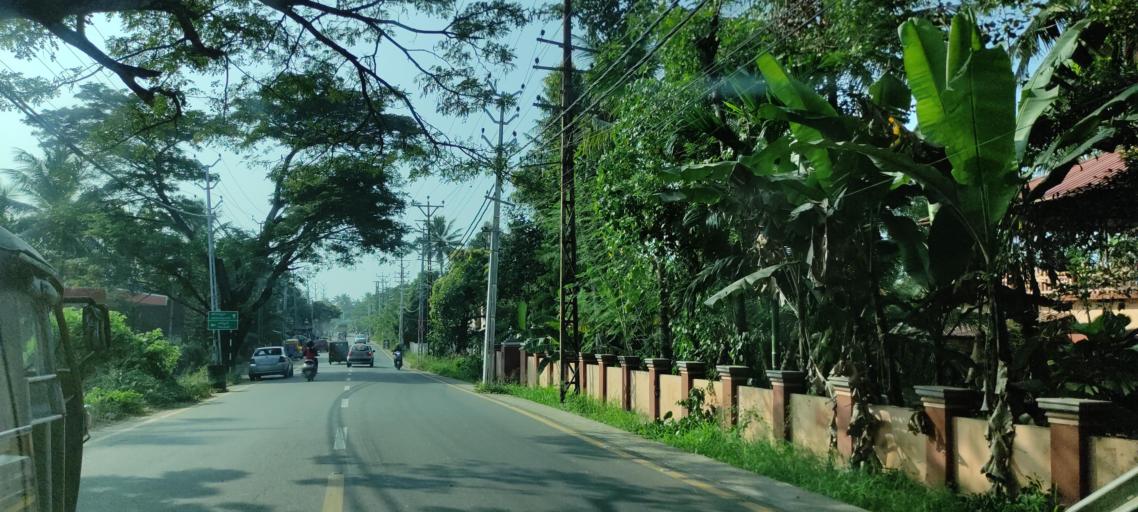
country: IN
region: Kerala
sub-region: Kottayam
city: Changanacheri
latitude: 9.3614
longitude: 76.4703
